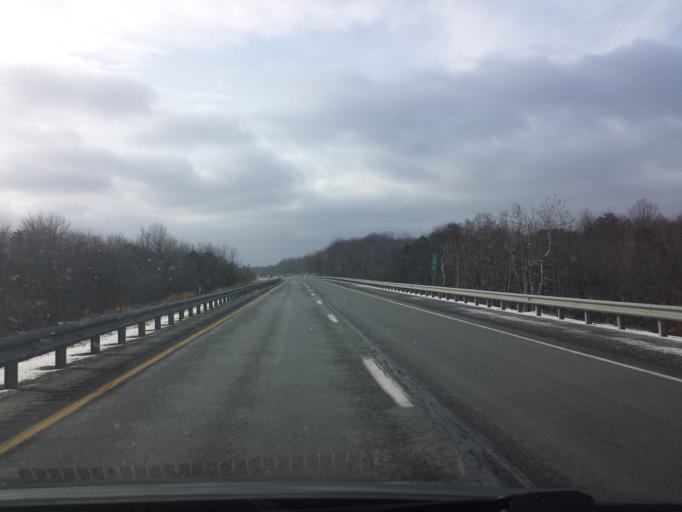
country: US
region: Pennsylvania
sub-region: Monroe County
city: Emerald Lakes
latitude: 41.0728
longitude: -75.4138
